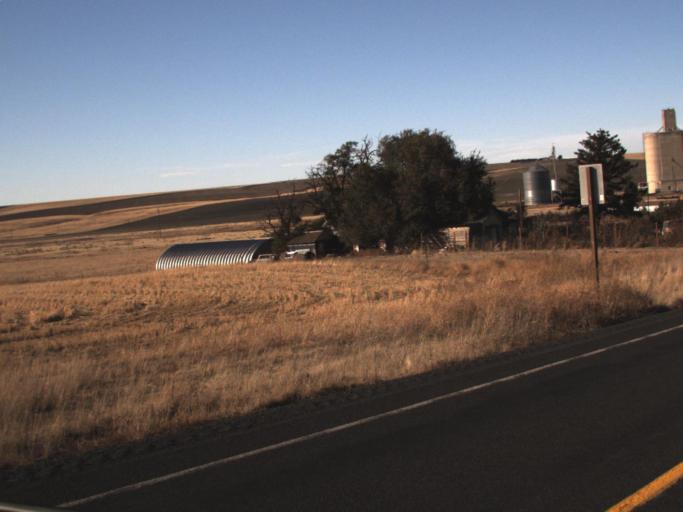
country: US
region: Washington
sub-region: Adams County
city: Ritzville
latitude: 46.9813
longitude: -118.3434
